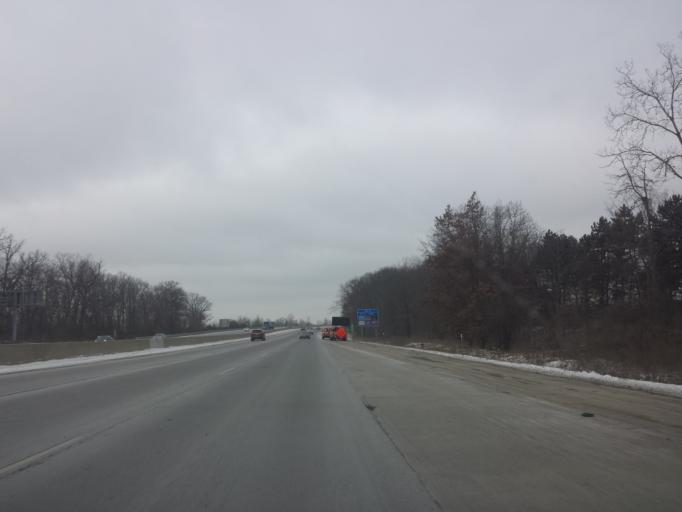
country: US
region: Michigan
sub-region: Oakland County
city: Rochester Hills
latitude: 42.6440
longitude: -83.1820
